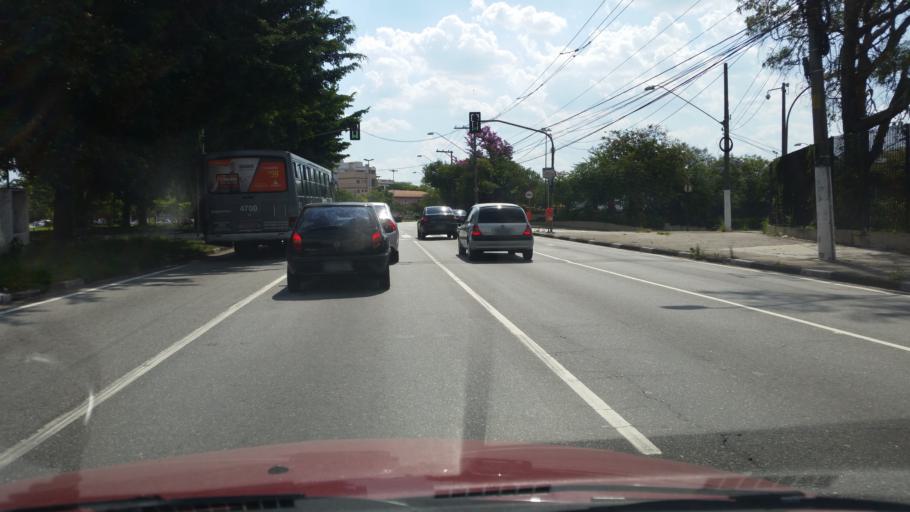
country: BR
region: Sao Paulo
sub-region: Sao Bernardo Do Campo
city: Sao Bernardo do Campo
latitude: -23.6674
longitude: -46.5788
